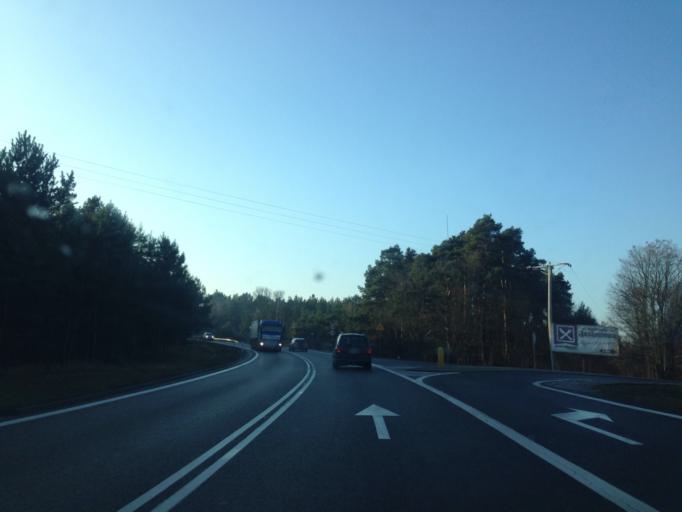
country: PL
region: Kujawsko-Pomorskie
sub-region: Powiat torunski
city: Zlawies Wielka
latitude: 53.0532
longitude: 18.3210
